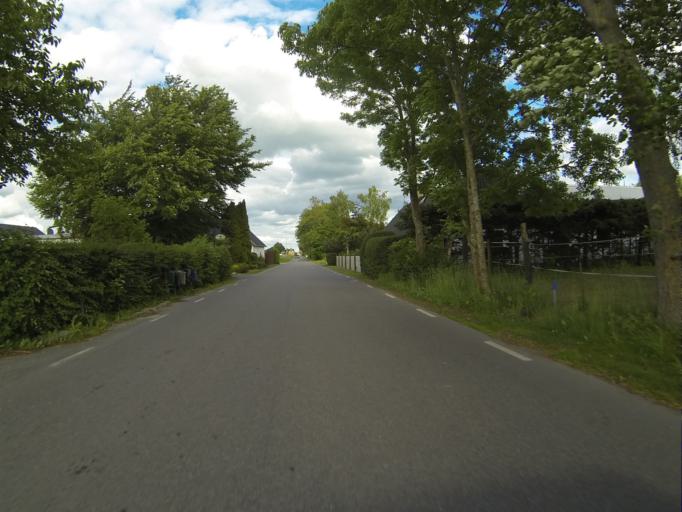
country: SE
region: Skane
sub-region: Staffanstorps Kommun
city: Staffanstorp
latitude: 55.6227
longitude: 13.2058
